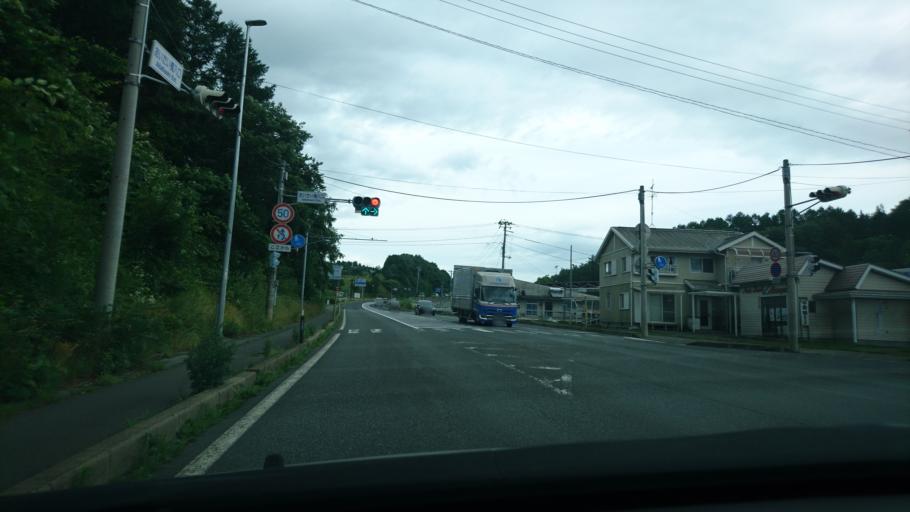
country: JP
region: Iwate
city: Ichinohe
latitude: 39.9671
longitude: 141.2126
